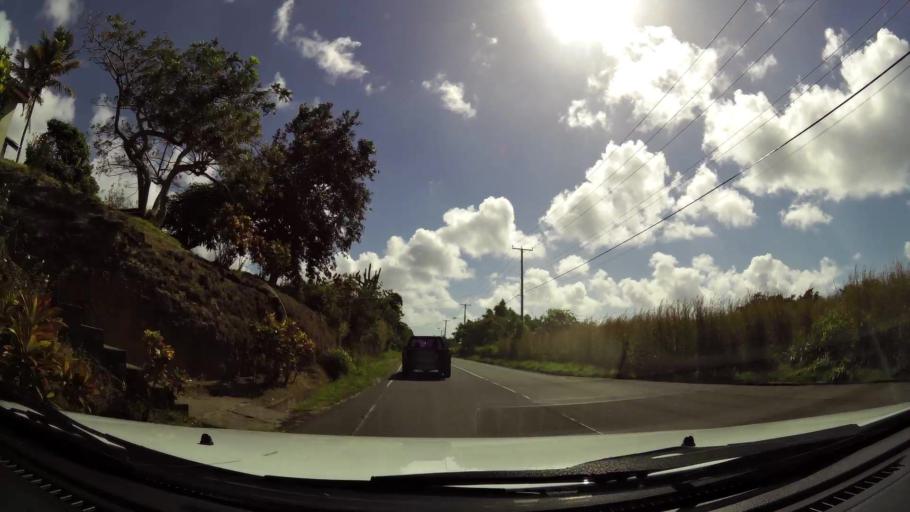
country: LC
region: Choiseul Quarter
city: Choiseul
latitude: 13.7634
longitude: -61.0329
